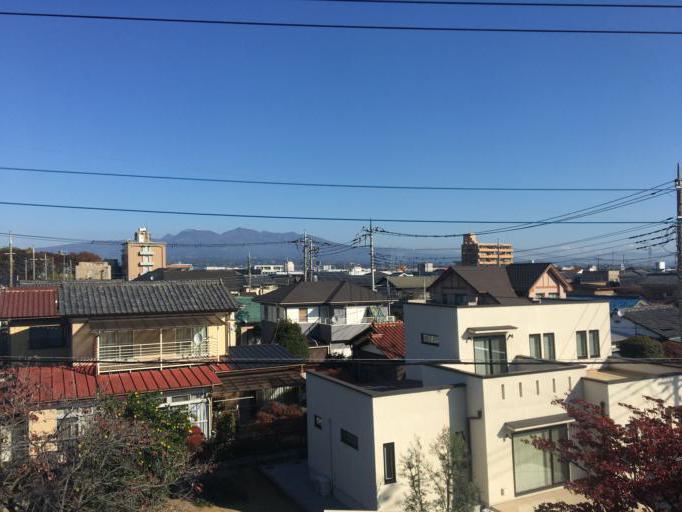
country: JP
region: Gunma
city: Maebashi-shi
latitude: 36.3802
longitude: 139.0935
